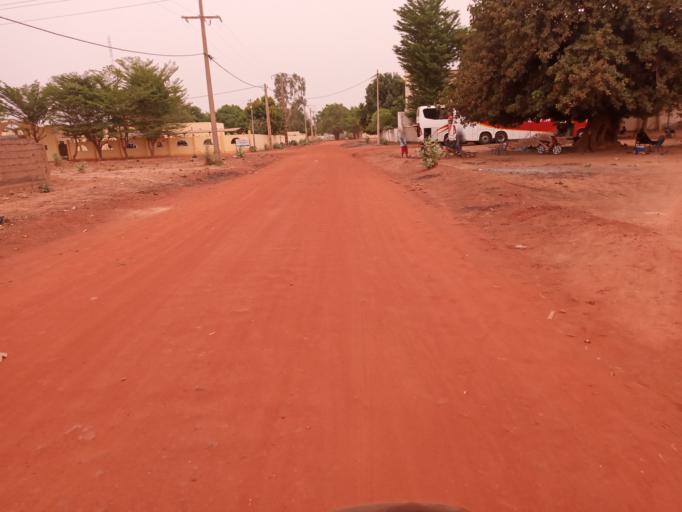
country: ML
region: Koulikoro
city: Koulikoro
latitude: 12.8420
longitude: -7.5861
